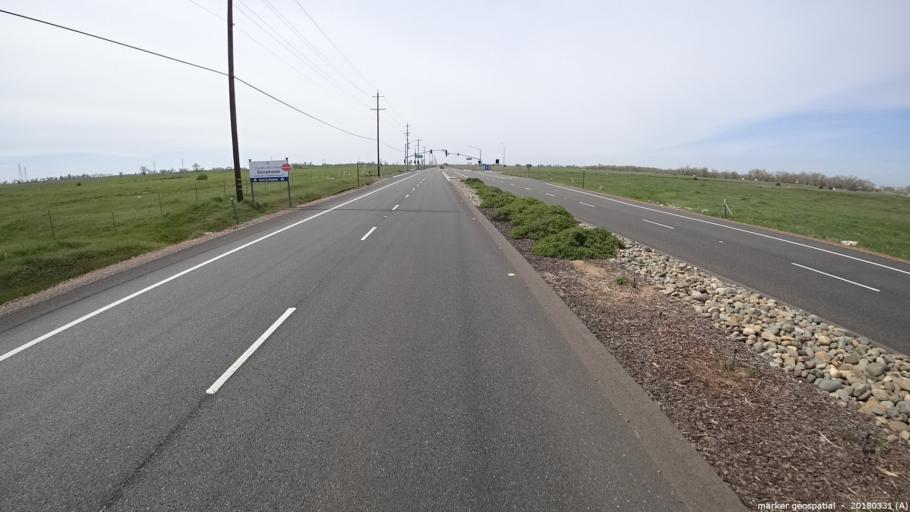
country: US
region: California
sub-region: Sacramento County
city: Gold River
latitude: 38.5955
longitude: -121.1772
